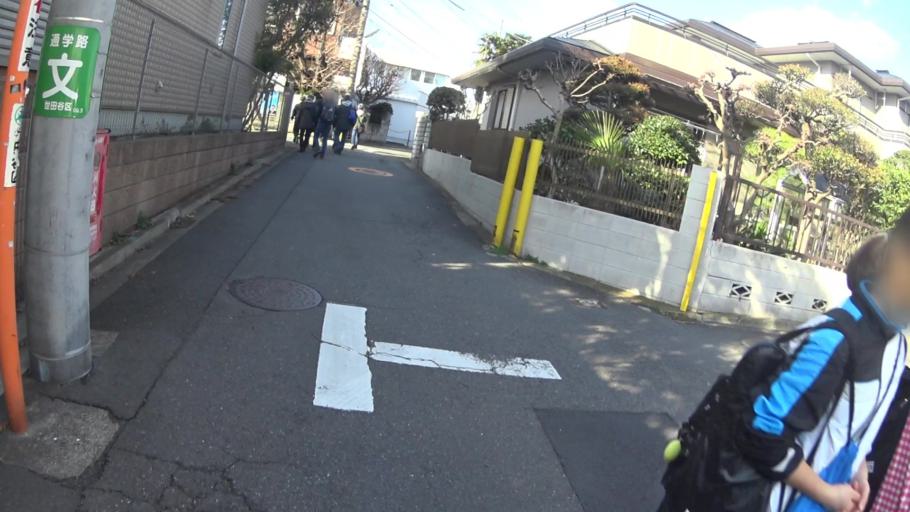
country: JP
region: Tokyo
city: Mitaka-shi
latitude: 35.6549
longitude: 139.6052
